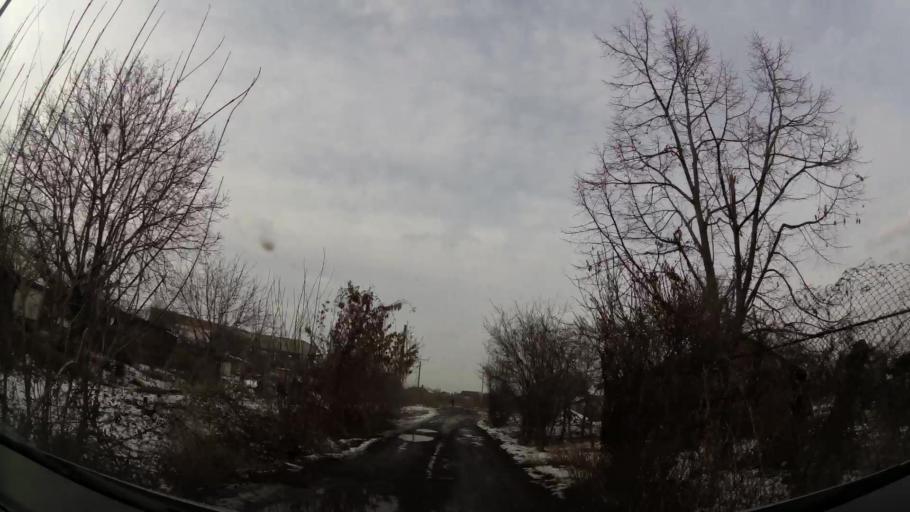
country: BG
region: Sofia-Capital
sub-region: Stolichna Obshtina
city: Sofia
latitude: 42.6951
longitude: 23.3808
